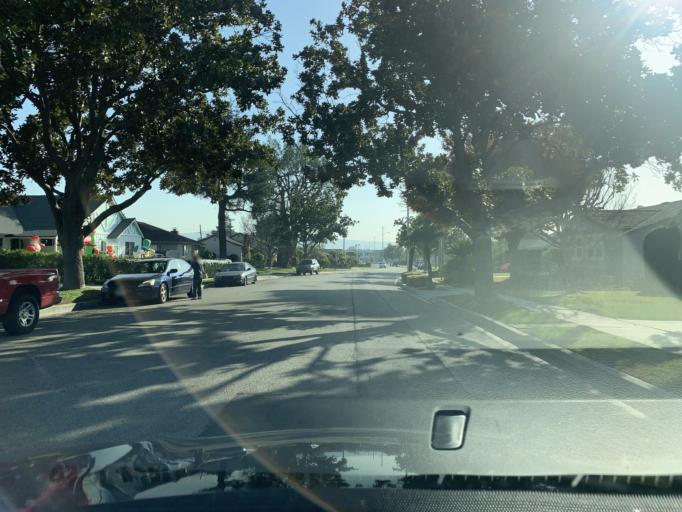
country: US
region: California
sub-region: Los Angeles County
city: Covina
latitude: 34.0817
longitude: -117.8971
